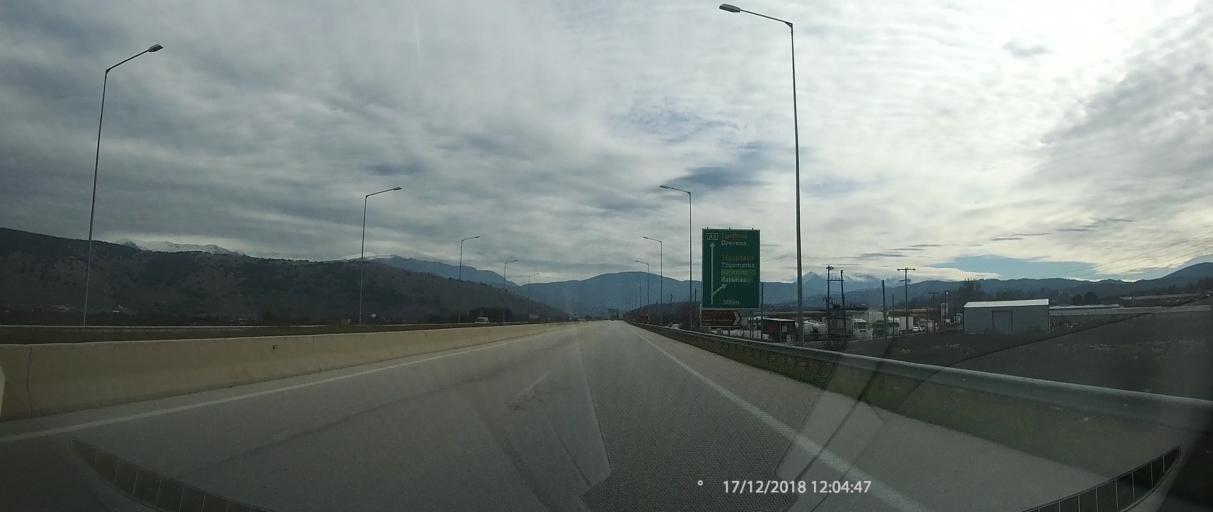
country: GR
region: Epirus
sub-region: Nomos Ioanninon
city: Katsikas
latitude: 39.6020
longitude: 20.8937
